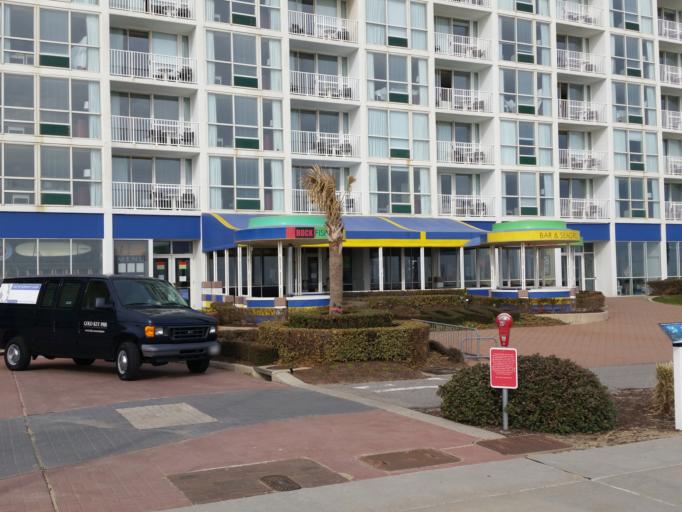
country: US
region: Virginia
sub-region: City of Virginia Beach
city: Virginia Beach
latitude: 36.8446
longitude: -75.9731
